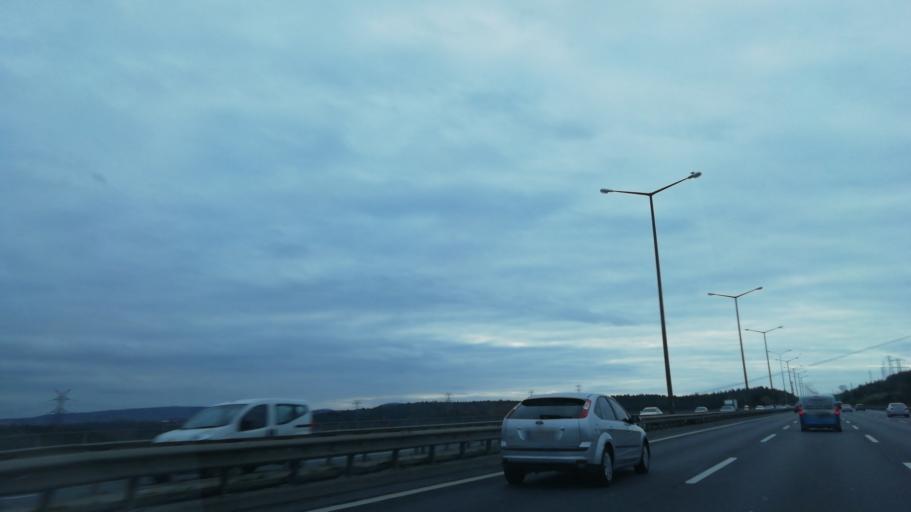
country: TR
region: Istanbul
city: Umraniye
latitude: 41.0761
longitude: 29.1000
